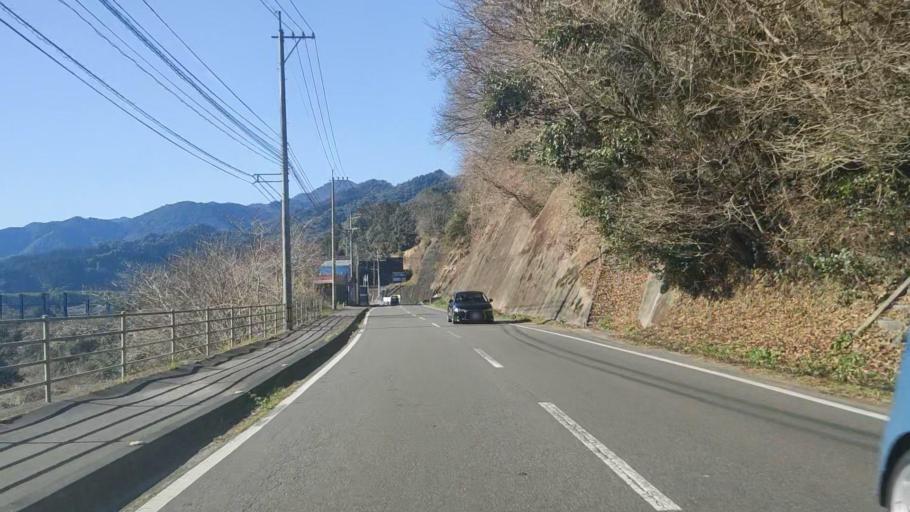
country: JP
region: Oita
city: Saiki
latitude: 32.9757
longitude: 131.8555
